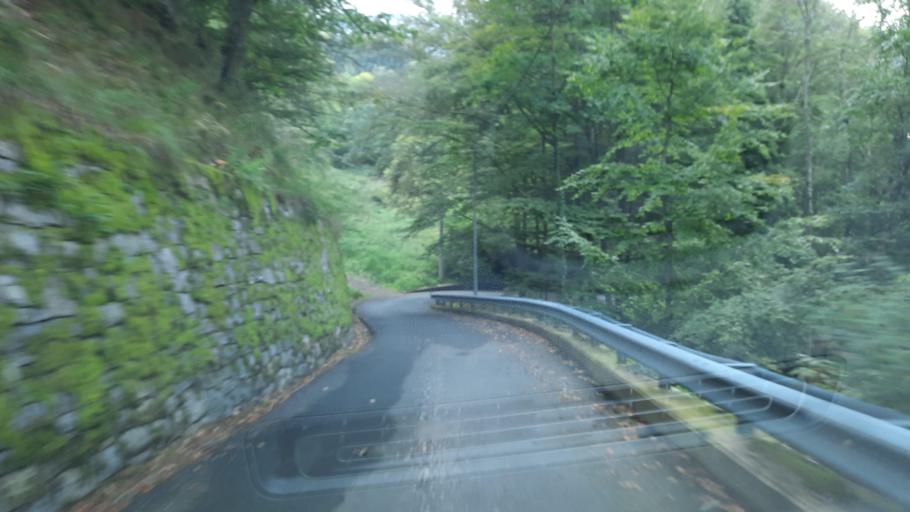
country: IT
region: Piedmont
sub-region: Provincia di Biella
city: Campiglia Cervo
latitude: 45.6573
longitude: 8.0024
